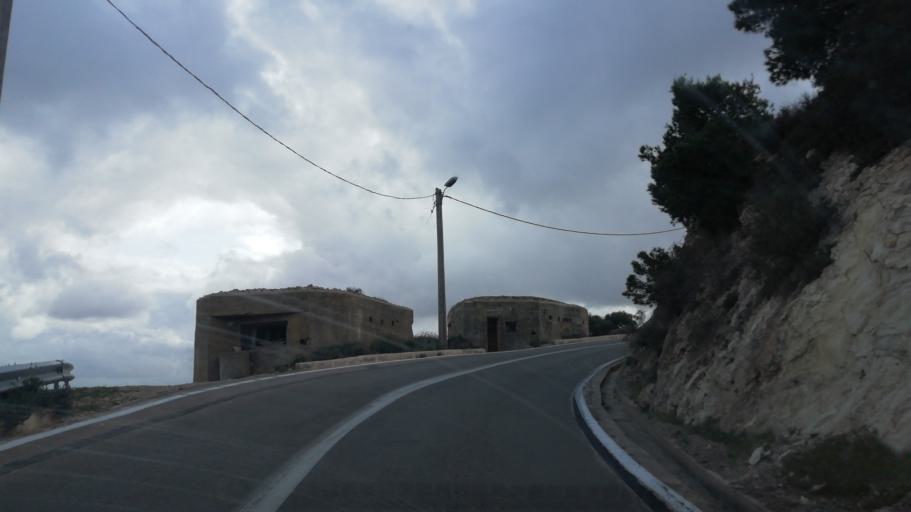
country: DZ
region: Oran
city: Oran
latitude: 35.7060
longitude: -0.6689
